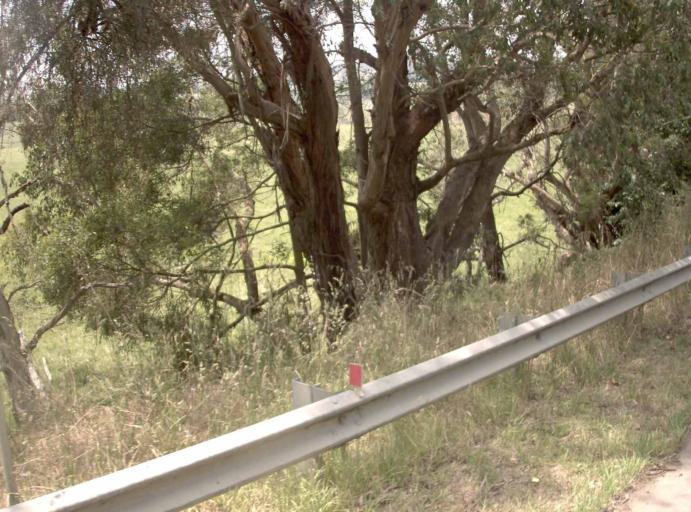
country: AU
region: Victoria
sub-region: Latrobe
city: Traralgon
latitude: -38.2877
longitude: 146.6994
